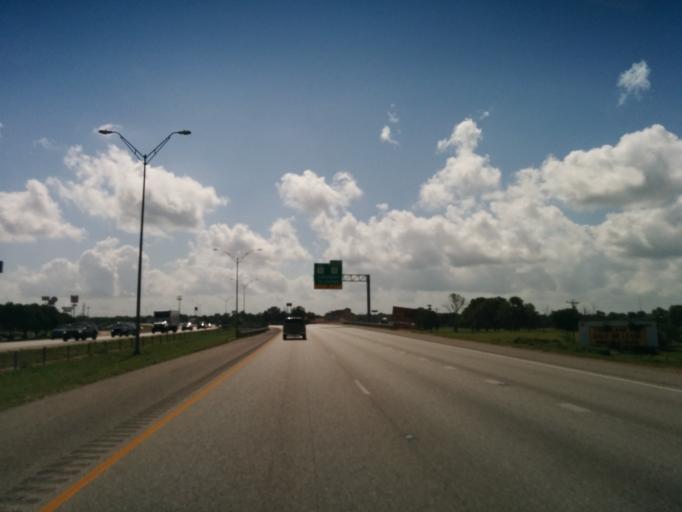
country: US
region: Texas
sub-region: Colorado County
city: Columbus
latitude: 29.6919
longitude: -96.5458
